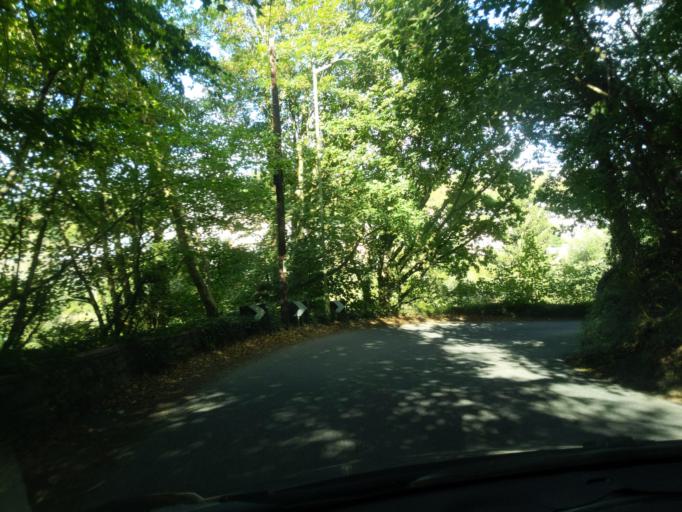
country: GB
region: England
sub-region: Devon
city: Great Torrington
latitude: 50.9472
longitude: -4.1568
